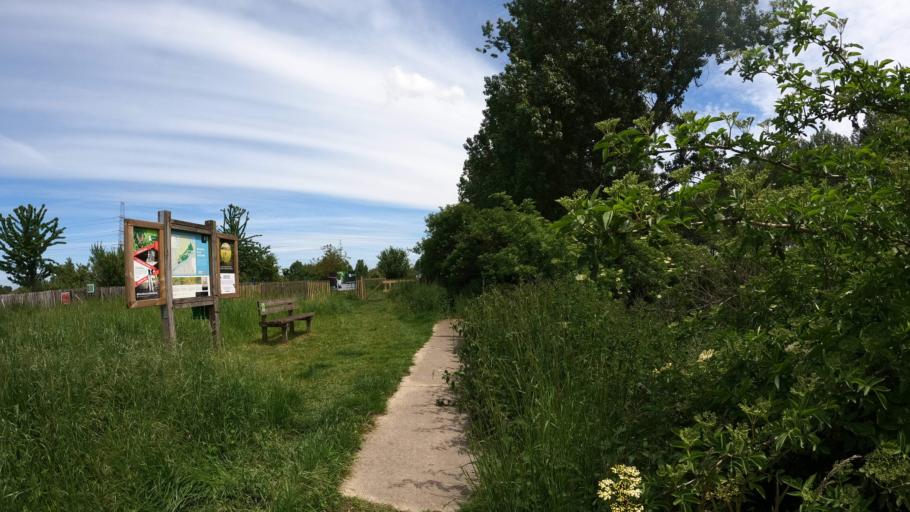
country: BE
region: Flanders
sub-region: Provincie Oost-Vlaanderen
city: Beveren
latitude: 51.2562
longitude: 4.2795
